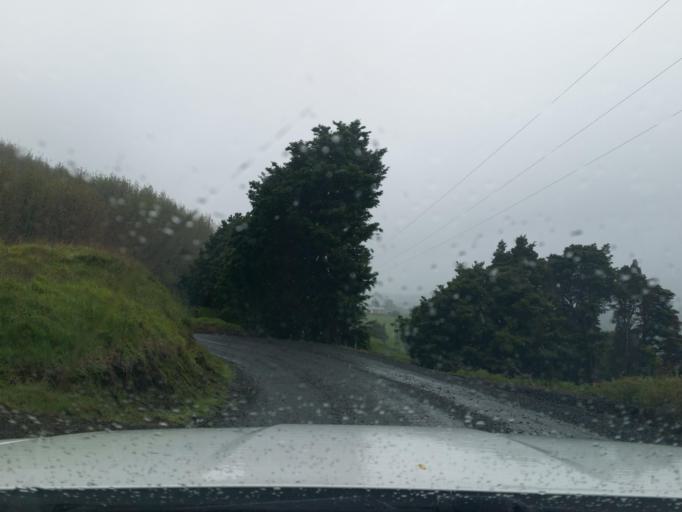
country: NZ
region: Northland
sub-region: Kaipara District
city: Dargaville
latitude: -35.7755
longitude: 173.9876
